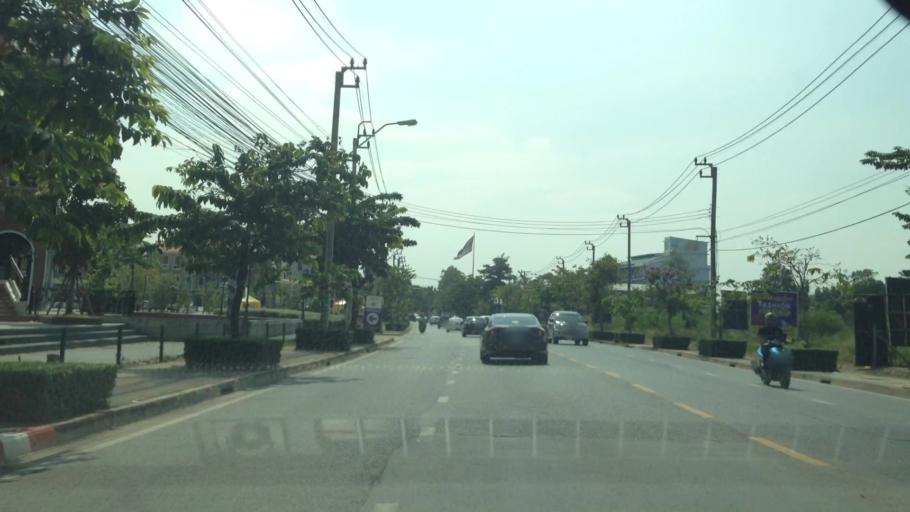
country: TH
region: Bangkok
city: Bang Khen
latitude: 13.8805
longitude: 100.6433
